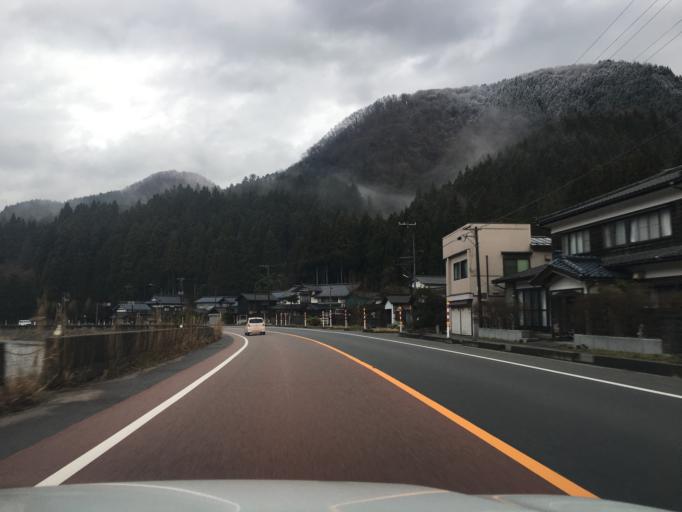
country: JP
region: Niigata
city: Murakami
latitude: 38.4734
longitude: 139.5523
